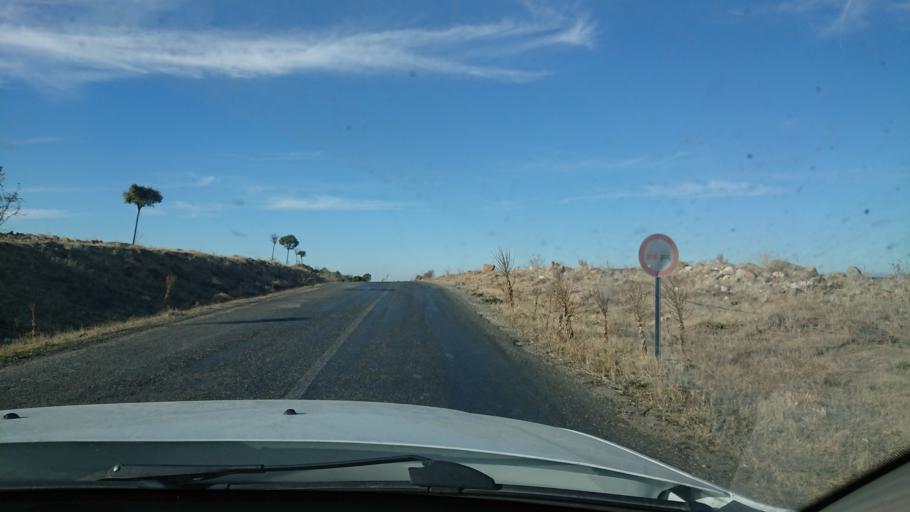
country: TR
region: Aksaray
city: Sariyahsi
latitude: 38.9688
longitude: 33.8688
